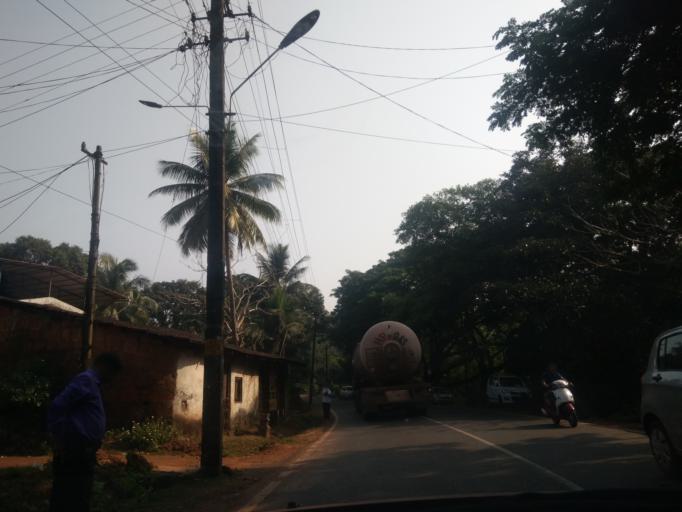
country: IN
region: Goa
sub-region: North Goa
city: Queula
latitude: 15.3683
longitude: 74.0085
